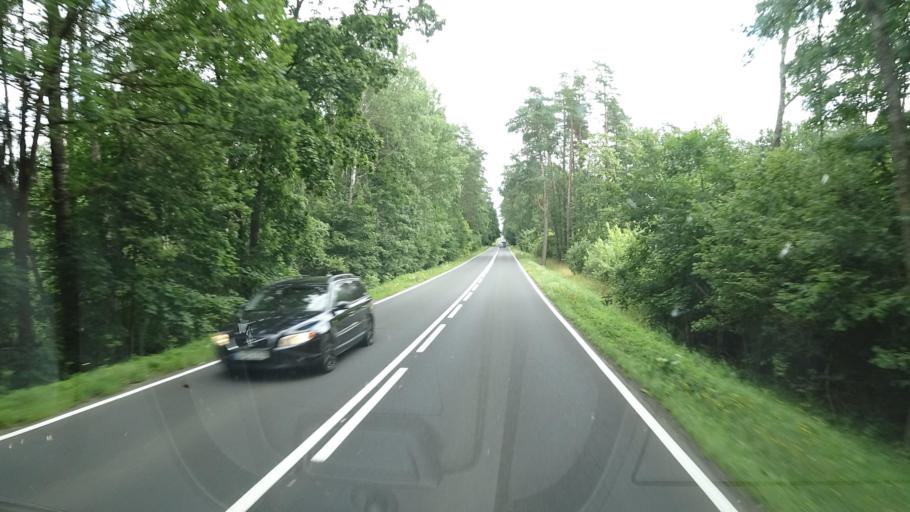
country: PL
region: Warmian-Masurian Voivodeship
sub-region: Powiat elcki
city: Stare Juchy
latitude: 53.7899
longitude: 22.1790
